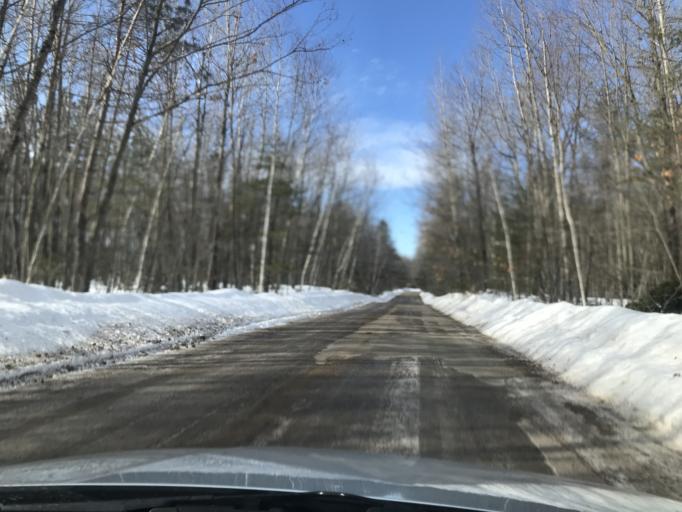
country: US
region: Wisconsin
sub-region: Menominee County
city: Legend Lake
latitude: 45.1129
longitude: -88.4388
